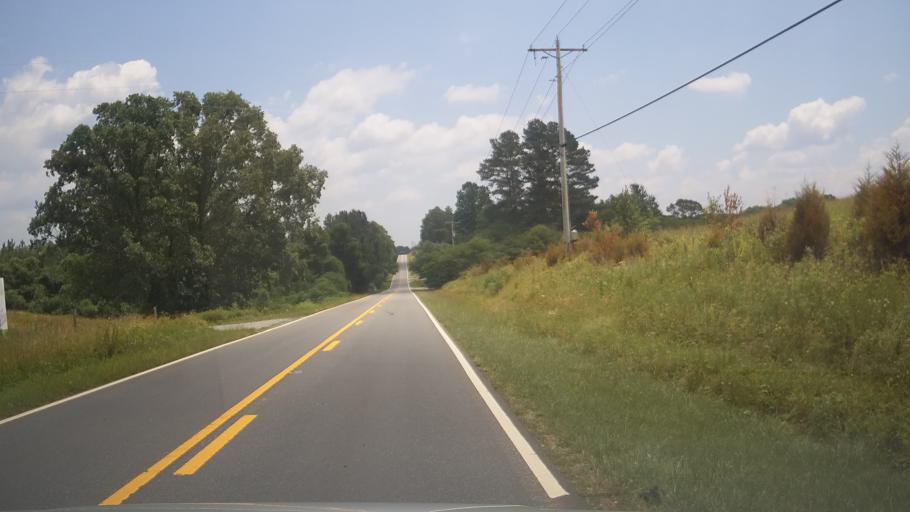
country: US
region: North Carolina
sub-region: Polk County
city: Columbus
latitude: 35.3195
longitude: -82.1233
